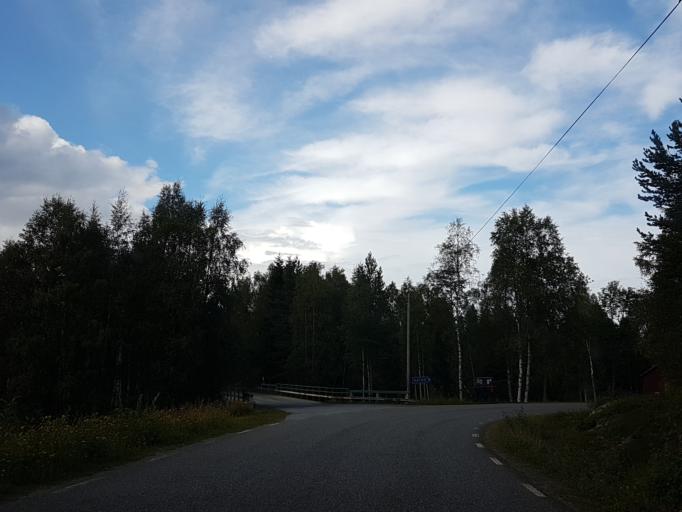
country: SE
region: Vaesterbotten
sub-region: Robertsfors Kommun
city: Robertsfors
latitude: 64.0366
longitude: 20.8511
